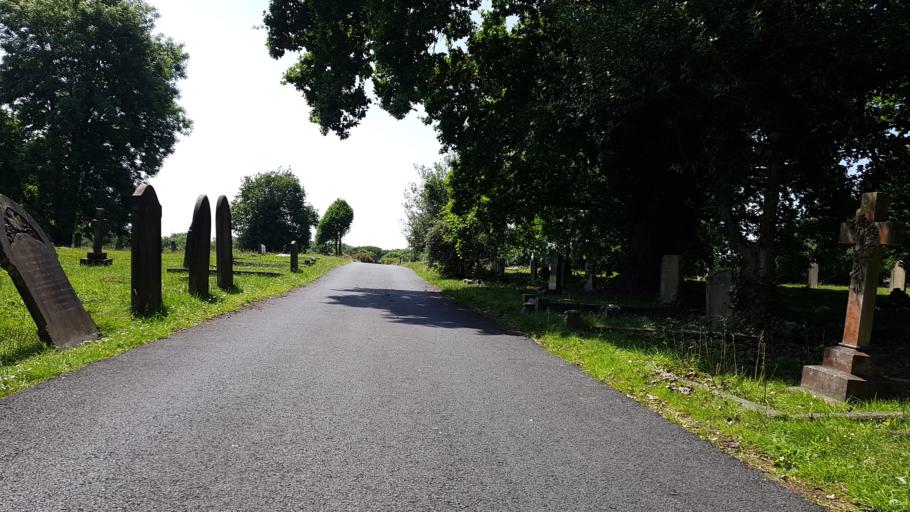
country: GB
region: England
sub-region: Isle of Wight
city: Cowes
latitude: 50.7498
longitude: -1.2999
